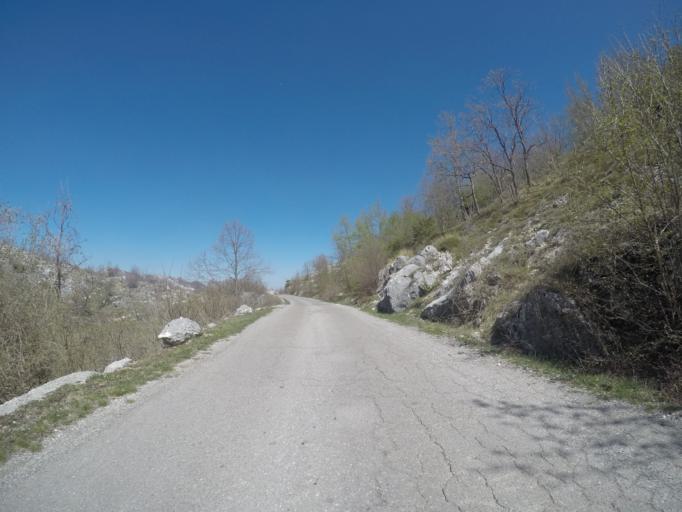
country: ME
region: Cetinje
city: Cetinje
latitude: 42.4434
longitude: 18.8742
